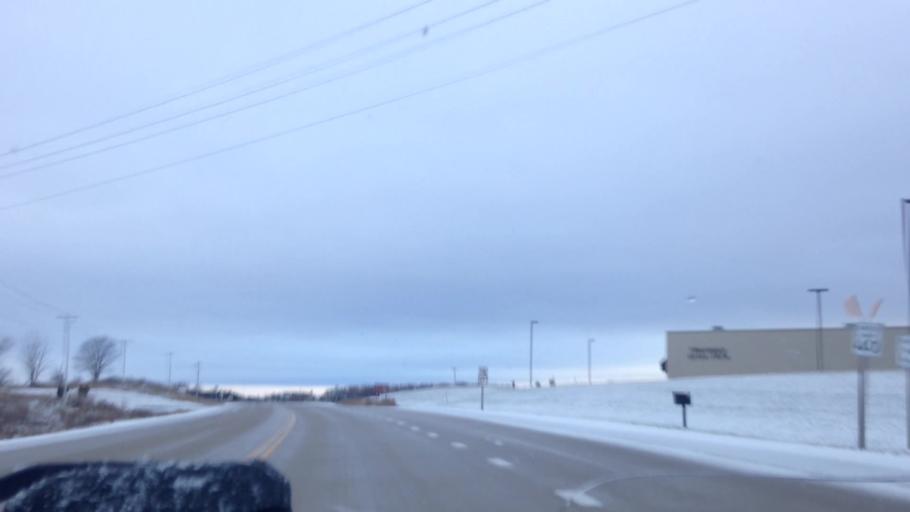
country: US
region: Wisconsin
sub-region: Dodge County
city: Mayville
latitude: 43.4937
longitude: -88.5681
